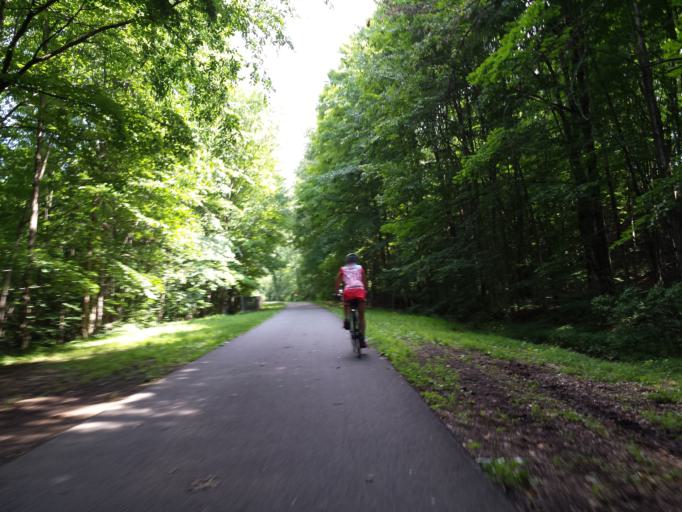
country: US
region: New York
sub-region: Saratoga County
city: Country Knolls
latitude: 42.9588
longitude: -73.8212
